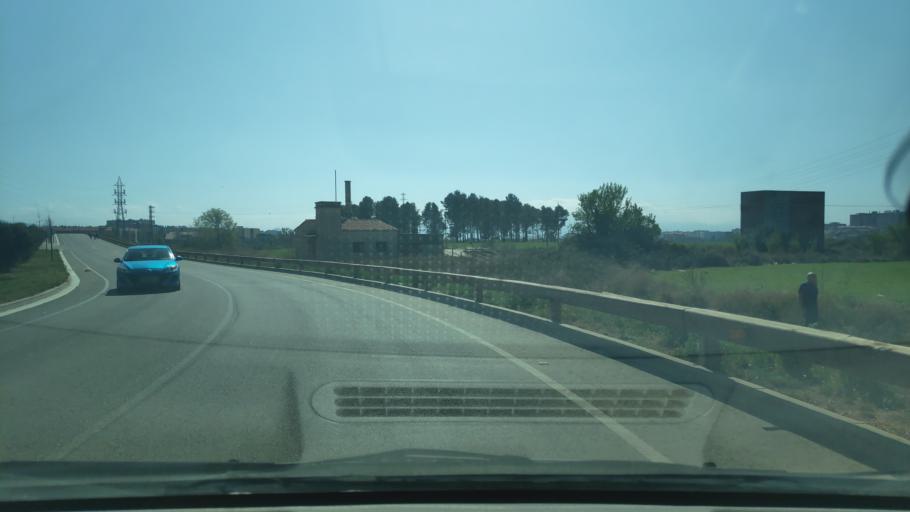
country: ES
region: Catalonia
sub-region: Provincia de Barcelona
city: Sabadell
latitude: 41.5564
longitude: 2.1213
